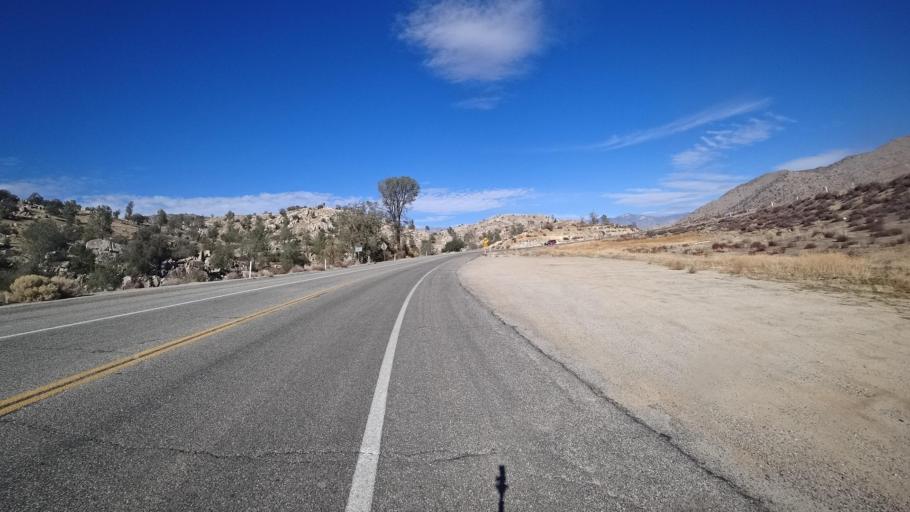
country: US
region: California
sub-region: Kern County
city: Lake Isabella
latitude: 35.6128
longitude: -118.4900
